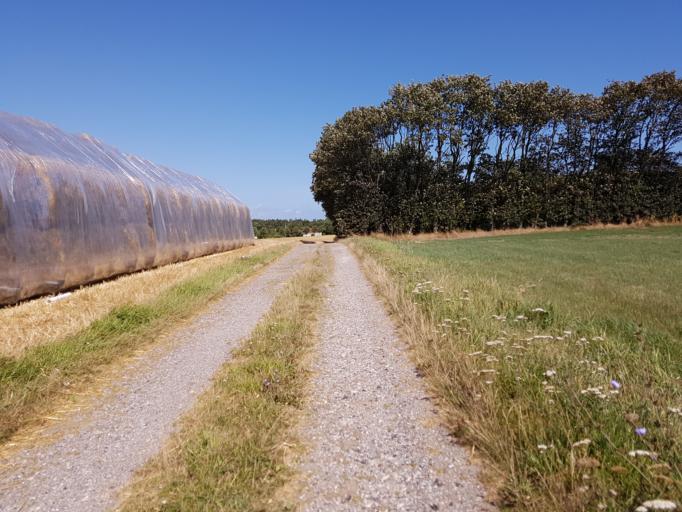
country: DK
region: Zealand
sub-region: Guldborgsund Kommune
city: Nykobing Falster
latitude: 54.5974
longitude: 11.9407
